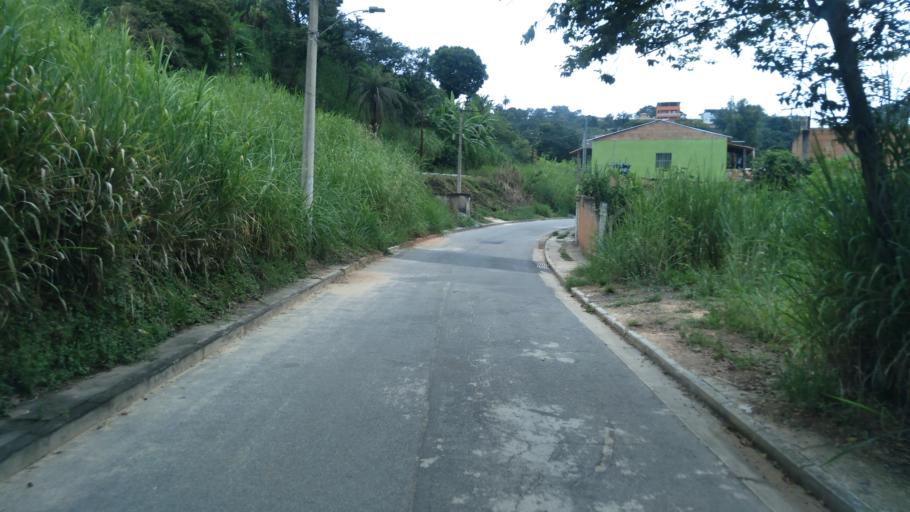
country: BR
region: Minas Gerais
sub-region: Santa Luzia
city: Santa Luzia
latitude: -19.8393
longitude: -43.8710
